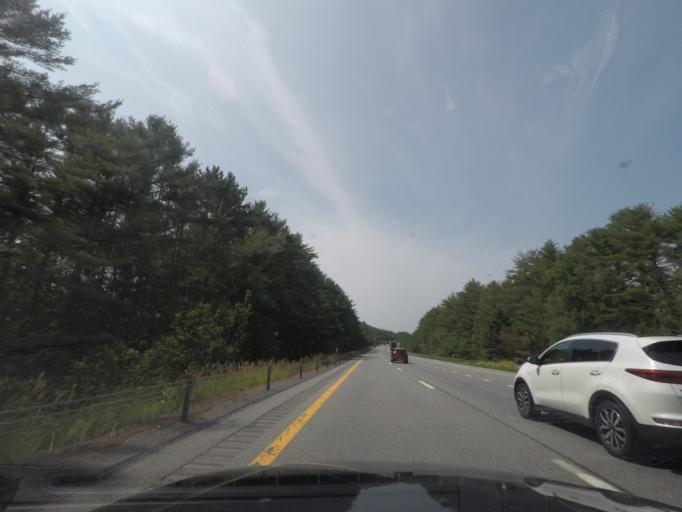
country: US
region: New York
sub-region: Warren County
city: Warrensburg
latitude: 43.6716
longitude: -73.7818
